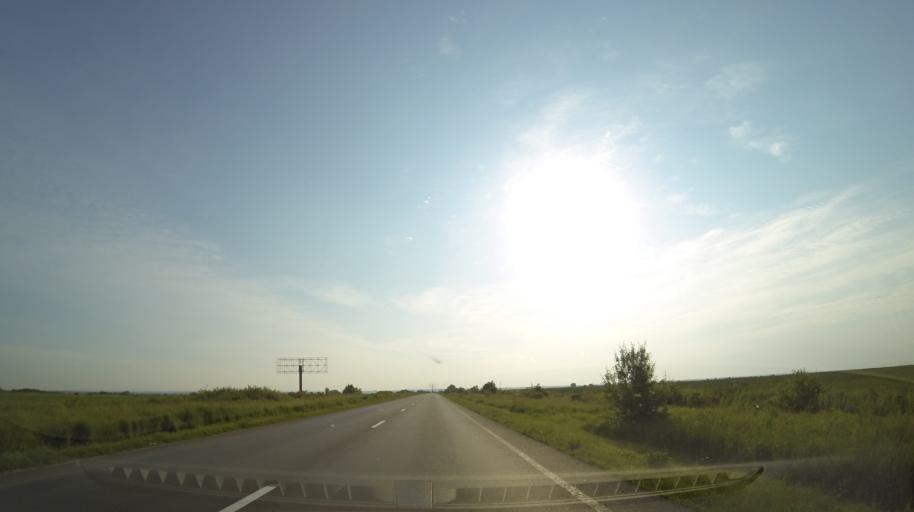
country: RO
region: Olt
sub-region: Comuna Piatra Olt
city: Piatra Olt
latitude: 44.3933
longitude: 24.2623
